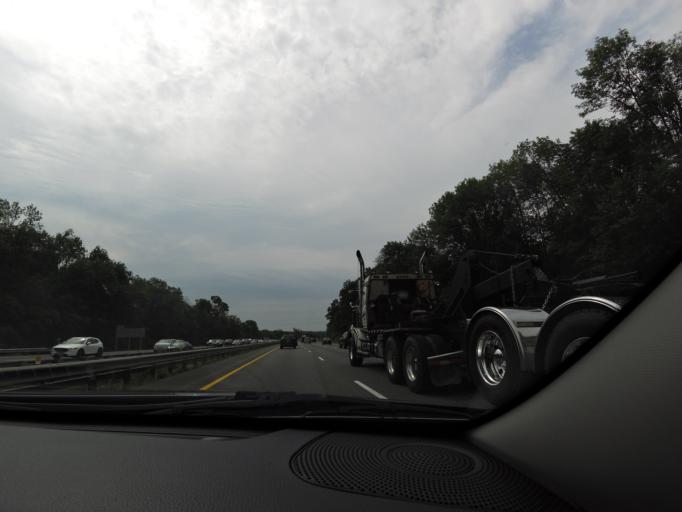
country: CA
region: Ontario
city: Bradford West Gwillimbury
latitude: 44.1865
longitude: -79.6473
